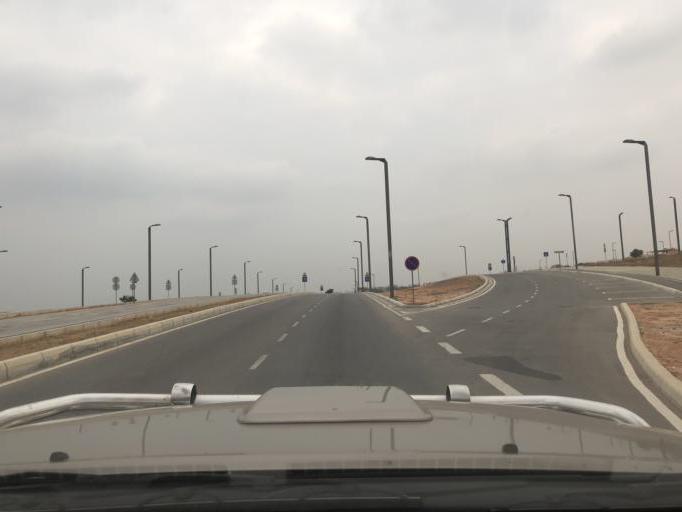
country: AO
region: Luanda
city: Luanda
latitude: -8.9043
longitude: 13.1733
